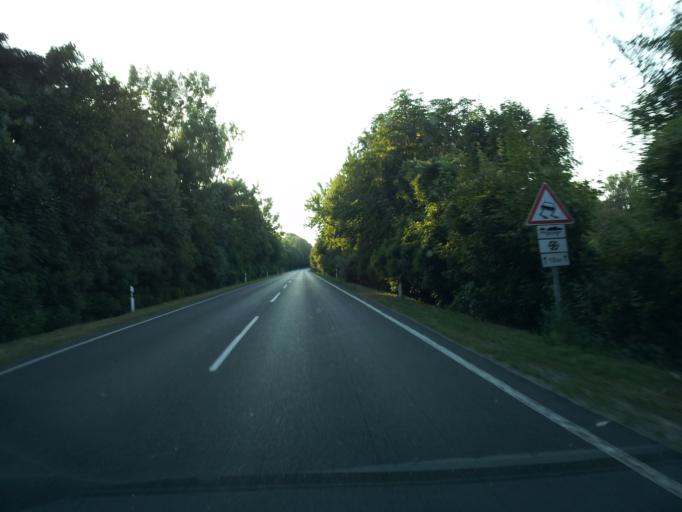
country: HU
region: Fejer
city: Szarliget
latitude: 47.5015
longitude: 18.4995
